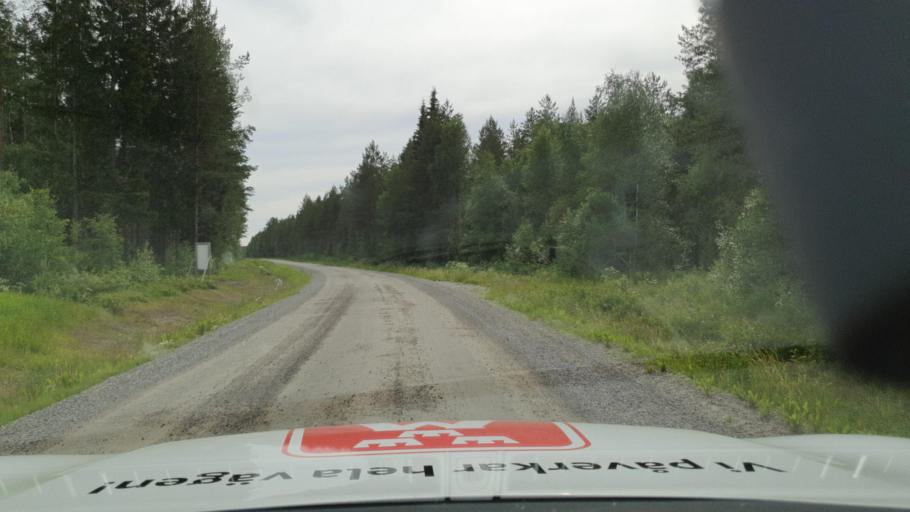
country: SE
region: Vaesterbotten
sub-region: Skelleftea Kommun
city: Burea
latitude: 64.4576
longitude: 21.0316
